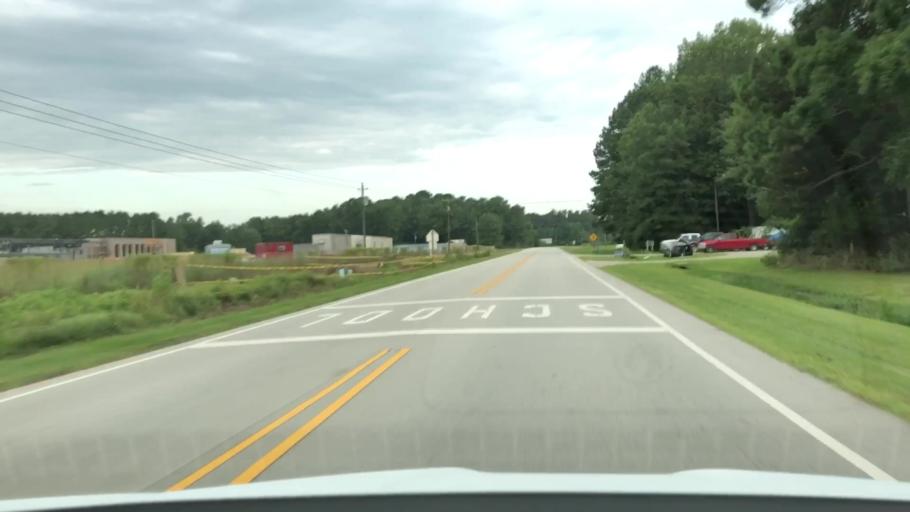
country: US
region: North Carolina
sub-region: Jones County
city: Trenton
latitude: 35.0353
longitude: -77.3360
